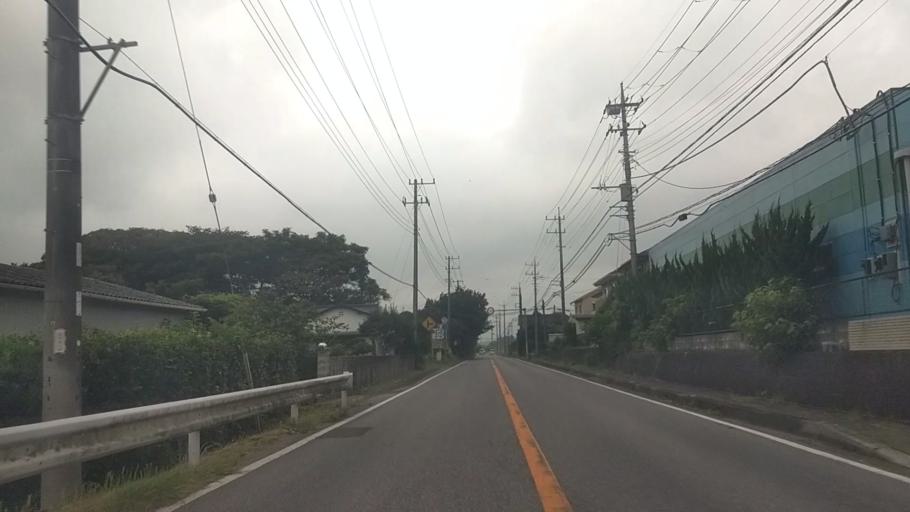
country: JP
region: Chiba
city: Kawaguchi
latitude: 35.1226
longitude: 140.0642
